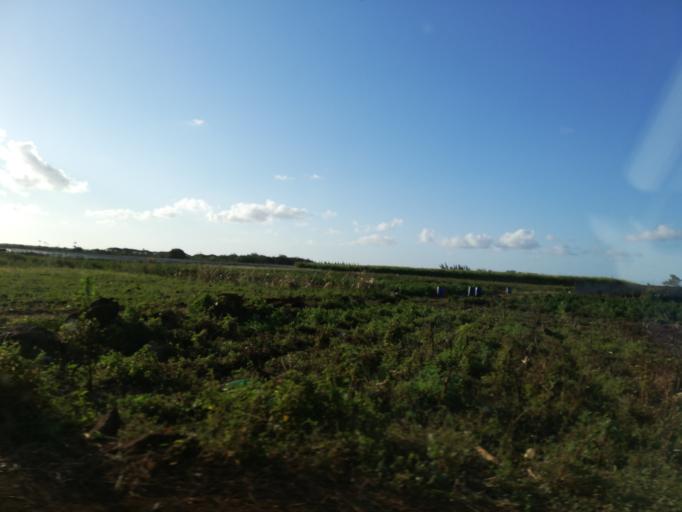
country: MU
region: Pamplemousses
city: Morcellemont Saint Andre
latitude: -20.0795
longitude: 57.5366
